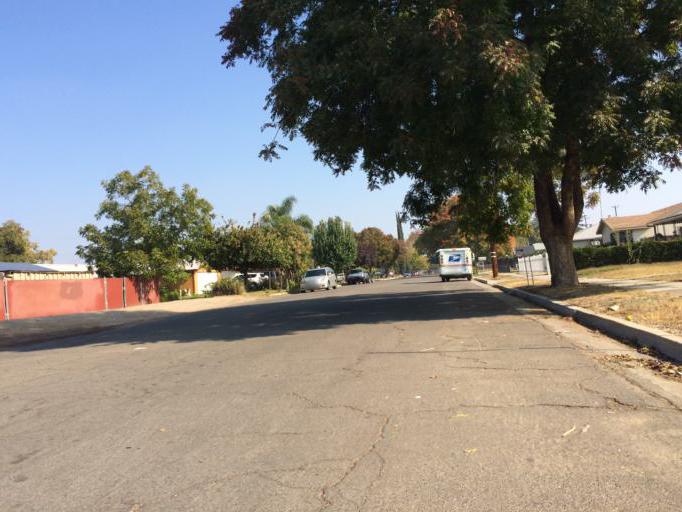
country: US
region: California
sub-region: Fresno County
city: Fresno
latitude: 36.7467
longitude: -119.7362
